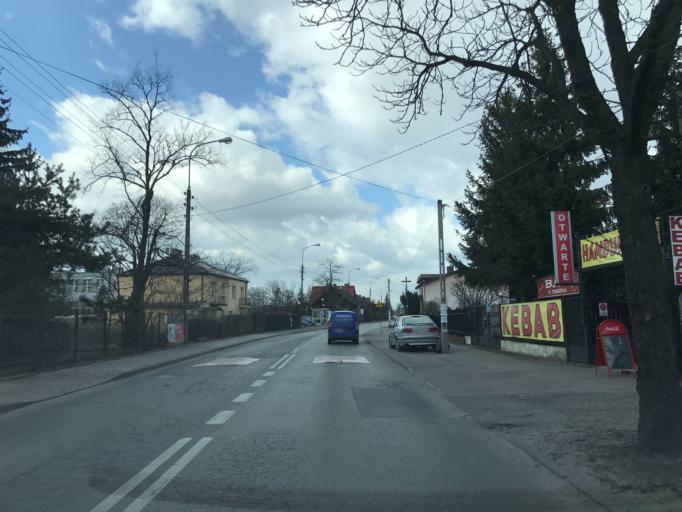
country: PL
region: Masovian Voivodeship
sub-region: Warszawa
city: Rembertow
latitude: 52.2625
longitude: 21.1580
